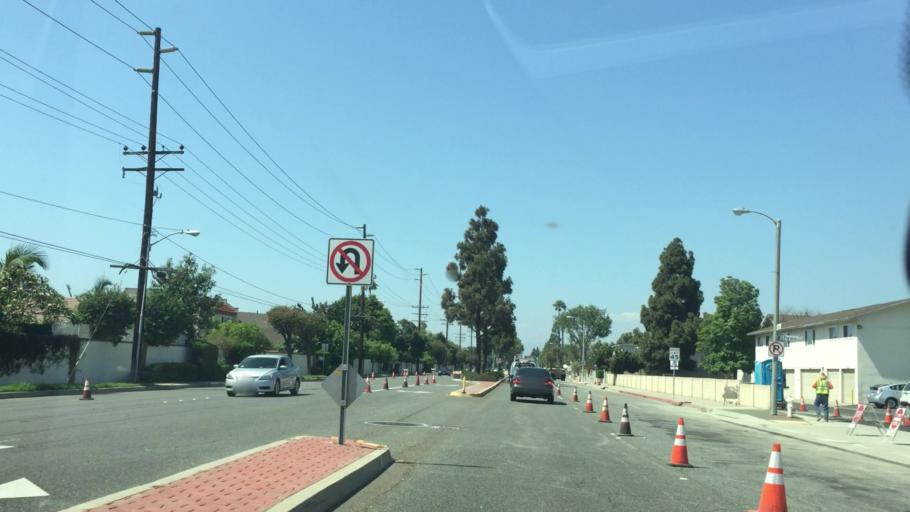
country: US
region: California
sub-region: Orange County
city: Fountain Valley
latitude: 33.7099
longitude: -117.9370
